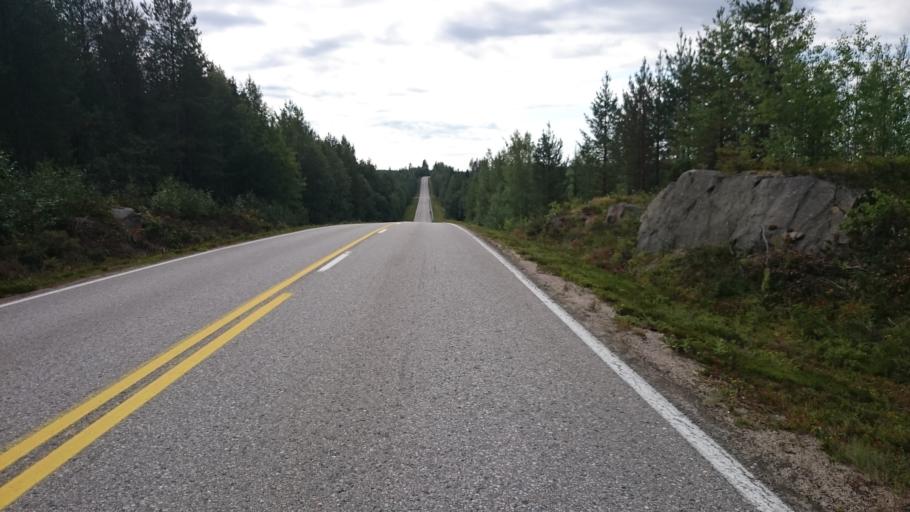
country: FI
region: Kainuu
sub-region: Kehys-Kainuu
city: Kuhmo
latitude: 64.4294
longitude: 29.8123
